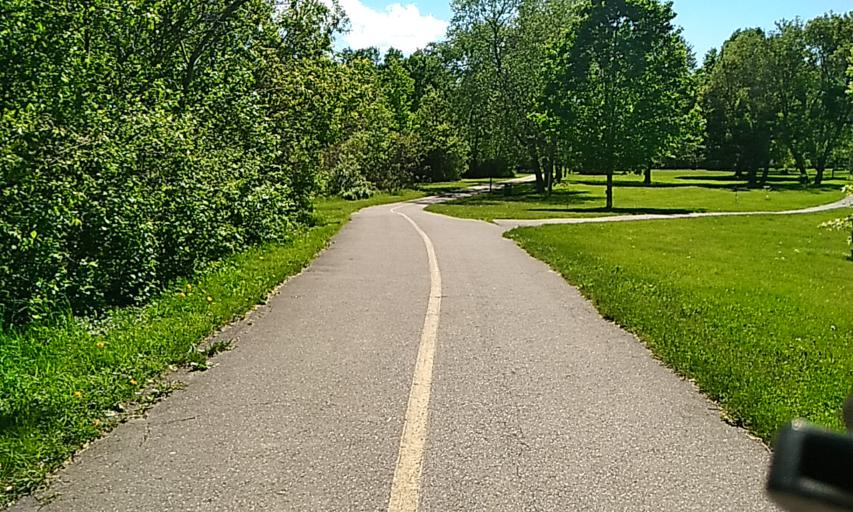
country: CA
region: Ontario
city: London
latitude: 42.9741
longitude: -81.2409
